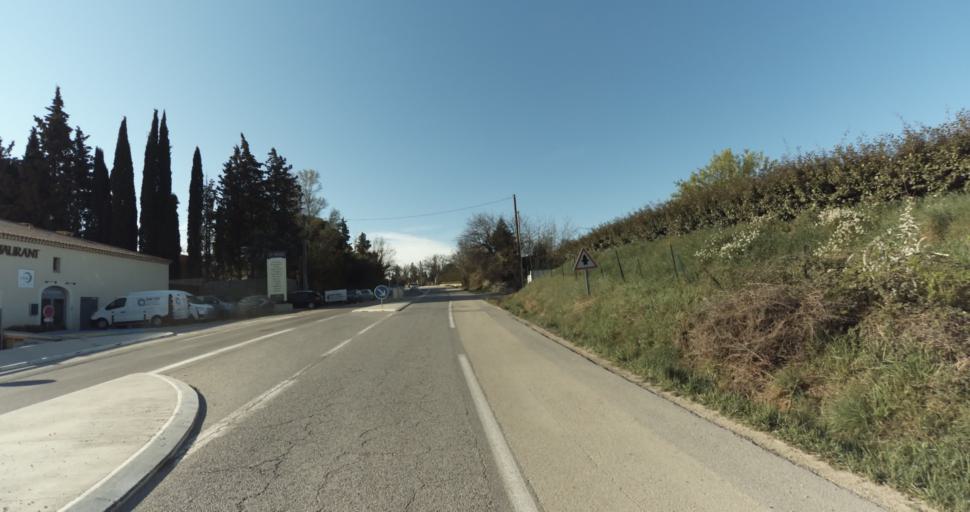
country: FR
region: Provence-Alpes-Cote d'Azur
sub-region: Departement des Bouches-du-Rhone
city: Aix-en-Provence
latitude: 43.5622
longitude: 5.4339
